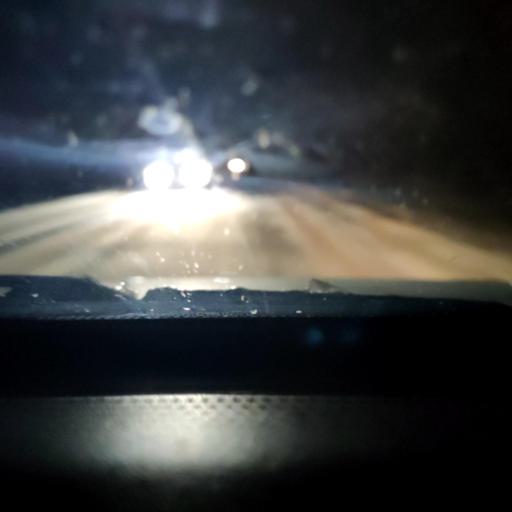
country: RU
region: Perm
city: Kondratovo
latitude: 57.9271
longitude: 56.0699
